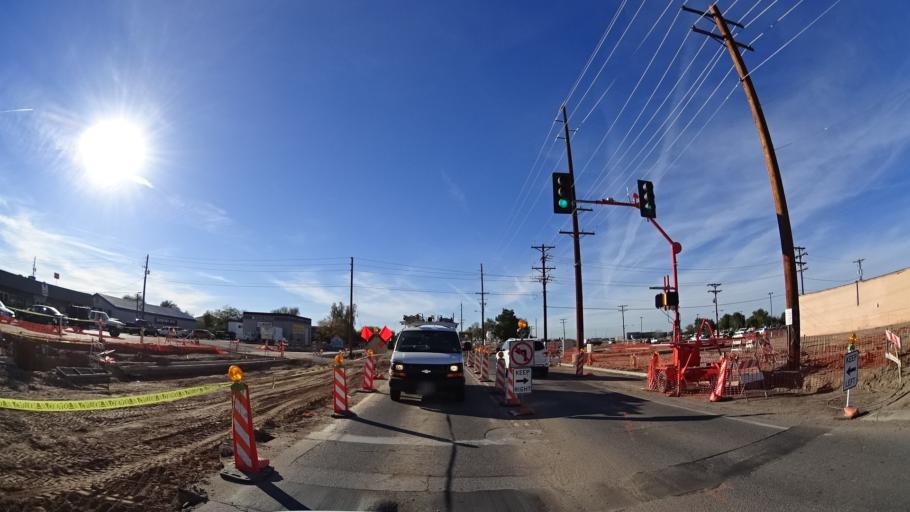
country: US
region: Arizona
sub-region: Maricopa County
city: Queen Creek
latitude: 33.2487
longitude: -111.6347
